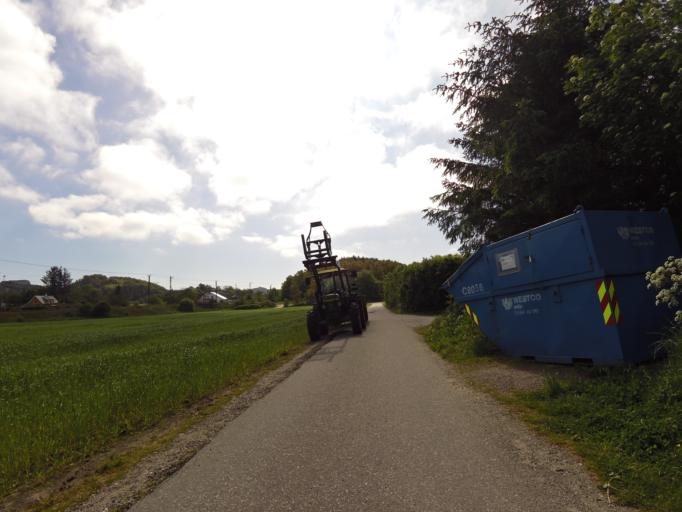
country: NO
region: Rogaland
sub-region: Ha
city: Vigrestad
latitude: 58.5214
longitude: 5.7978
